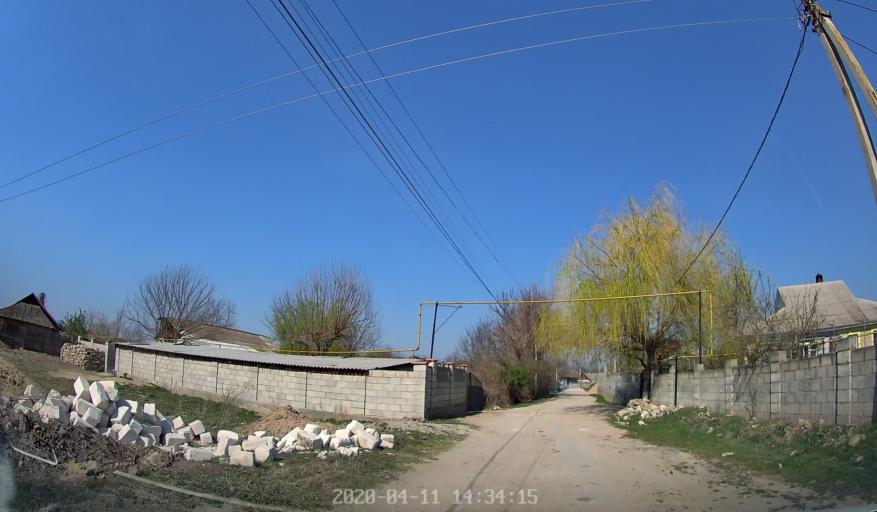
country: MD
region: Chisinau
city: Vadul lui Voda
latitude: 47.1011
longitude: 29.1728
